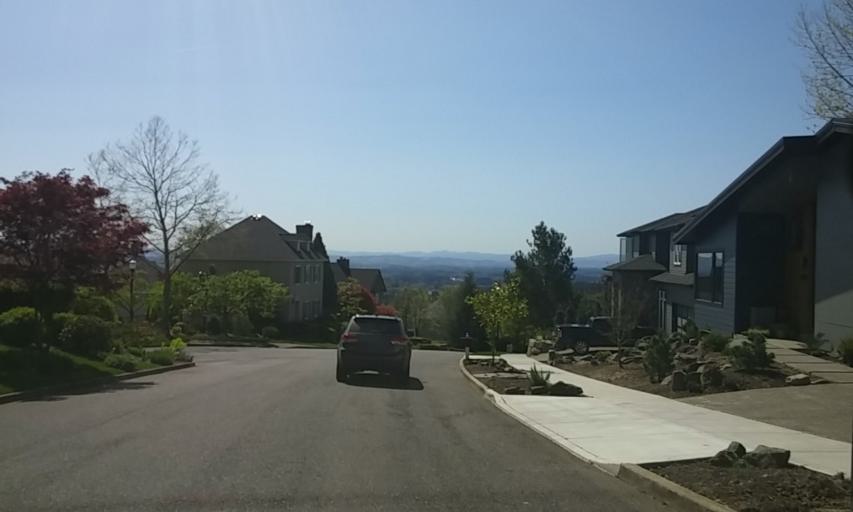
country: US
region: Oregon
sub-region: Washington County
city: West Haven
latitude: 45.5356
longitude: -122.7649
